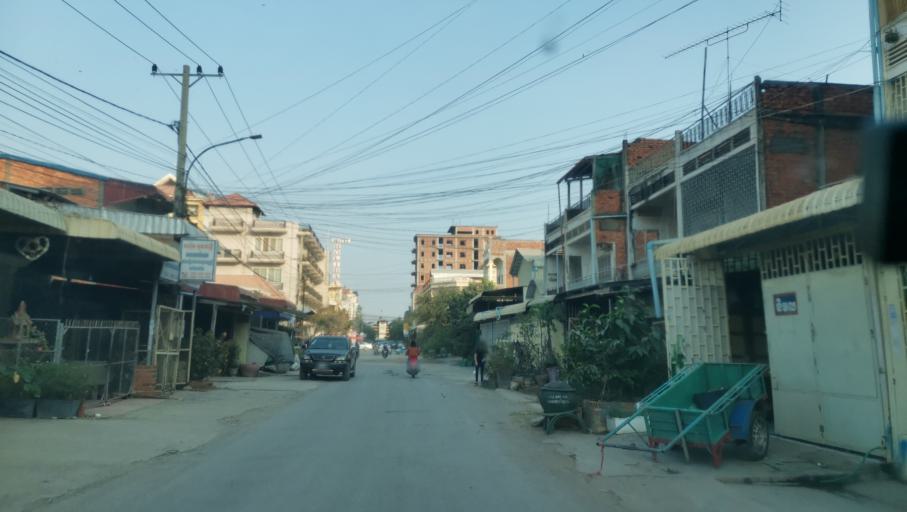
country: KH
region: Battambang
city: Battambang
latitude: 13.1028
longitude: 103.1947
